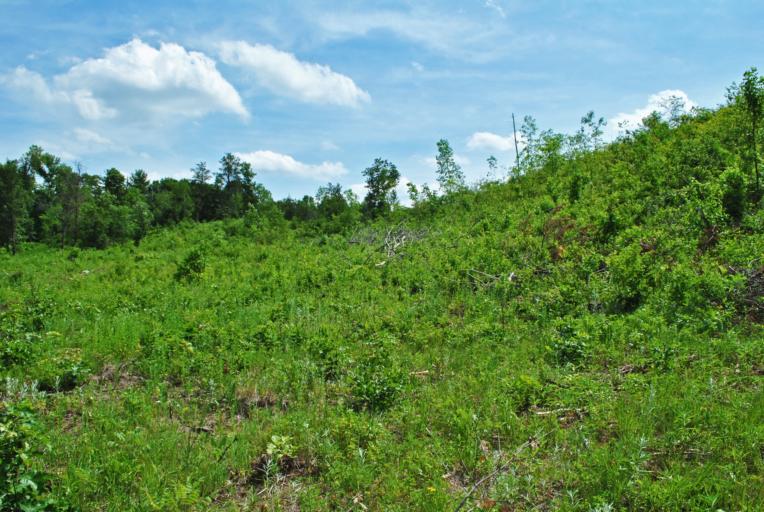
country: US
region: Wisconsin
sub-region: Dunn County
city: Menomonie
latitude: 44.7371
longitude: -91.8677
